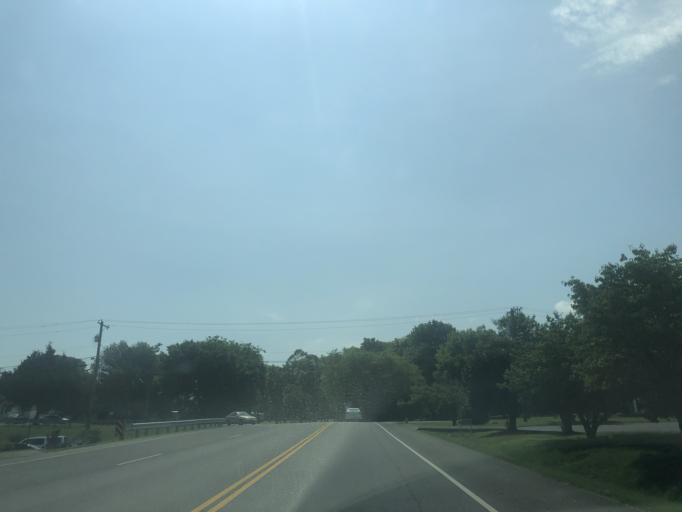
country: US
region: Tennessee
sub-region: Rutherford County
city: La Vergne
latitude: 36.0146
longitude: -86.5932
